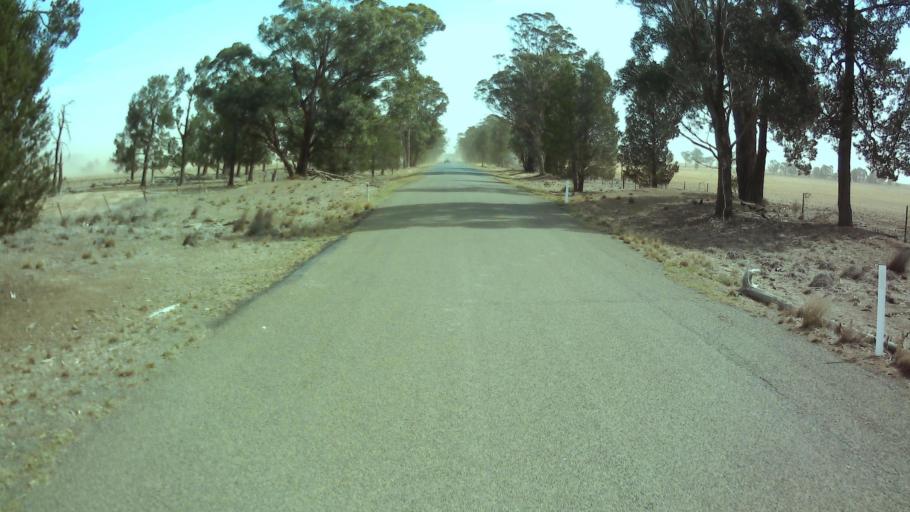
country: AU
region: New South Wales
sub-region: Weddin
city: Grenfell
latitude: -33.7555
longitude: 147.9898
